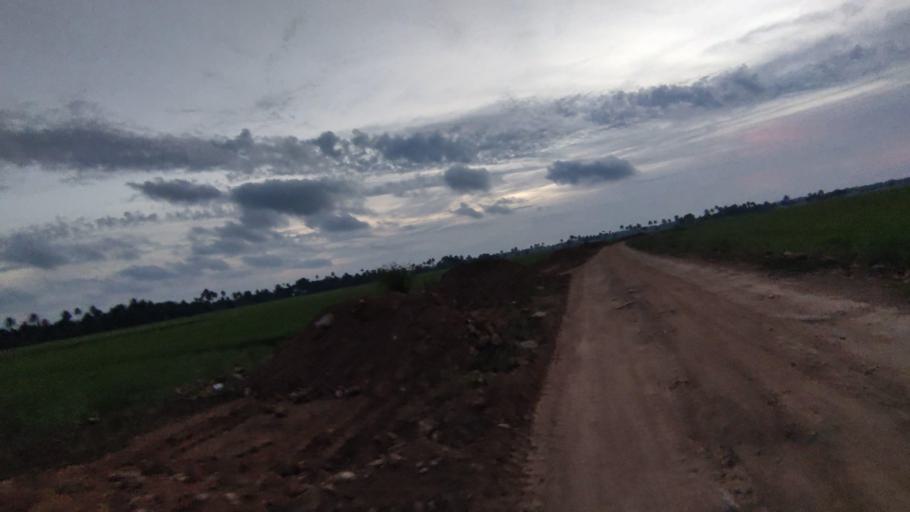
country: IN
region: Kerala
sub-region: Kottayam
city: Kottayam
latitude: 9.6434
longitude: 76.4462
